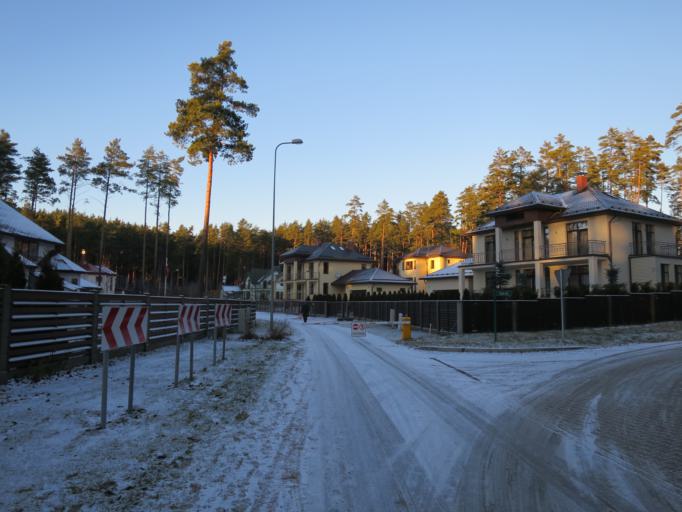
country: LV
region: Riga
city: Bergi
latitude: 56.9789
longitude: 24.3116
